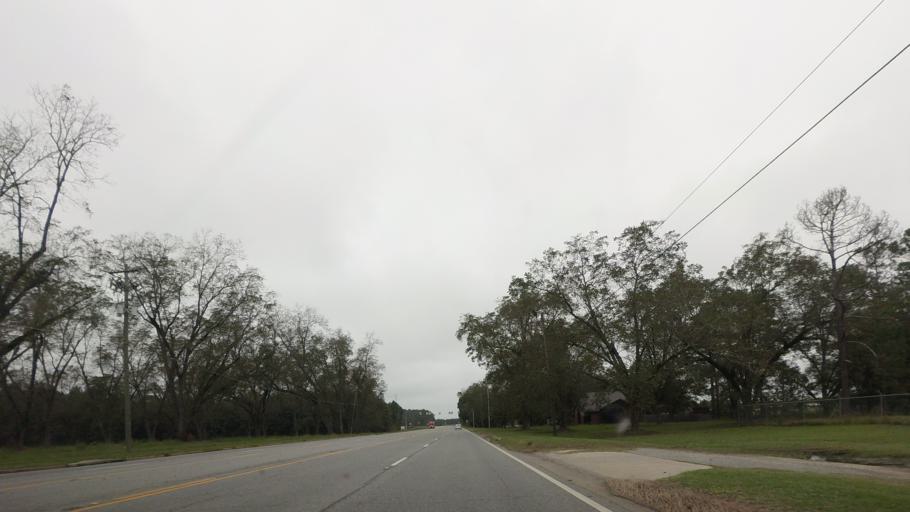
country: US
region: Georgia
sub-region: Berrien County
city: Enigma
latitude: 31.3888
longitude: -83.2282
